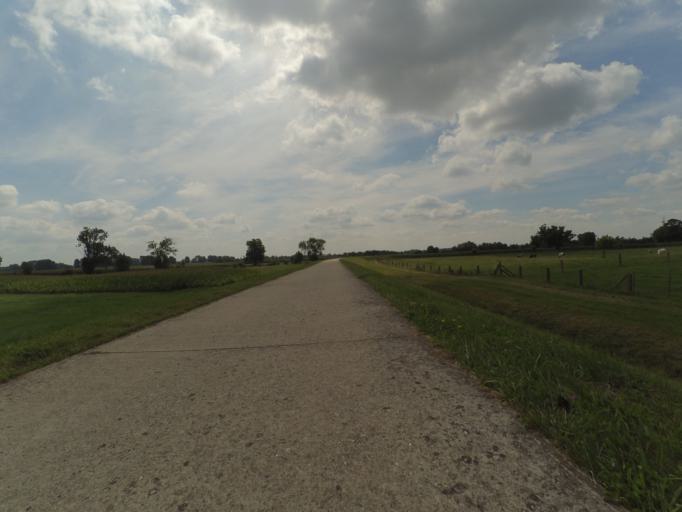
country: BE
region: Flanders
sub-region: Provincie Limburg
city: Maaseik
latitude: 51.0630
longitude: 5.7674
